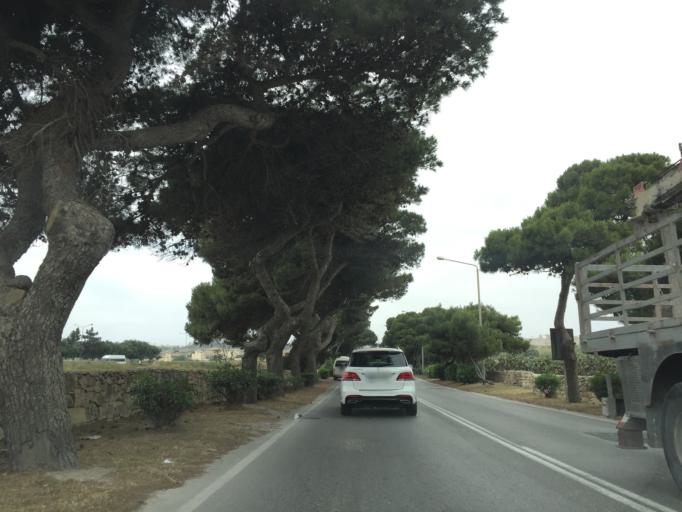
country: MT
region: L-Imdina
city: Imdina
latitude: 35.8841
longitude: 14.4175
